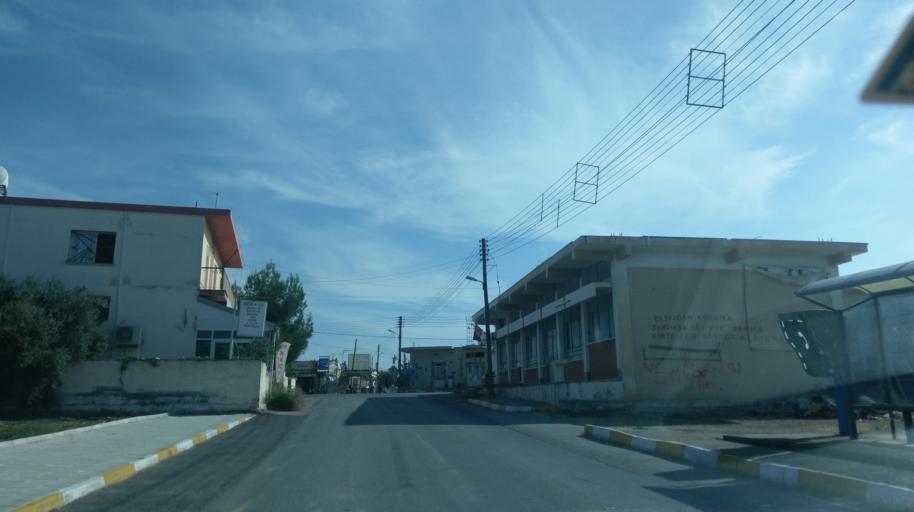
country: CY
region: Larnaka
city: Pergamos
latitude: 35.1053
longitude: 33.7160
